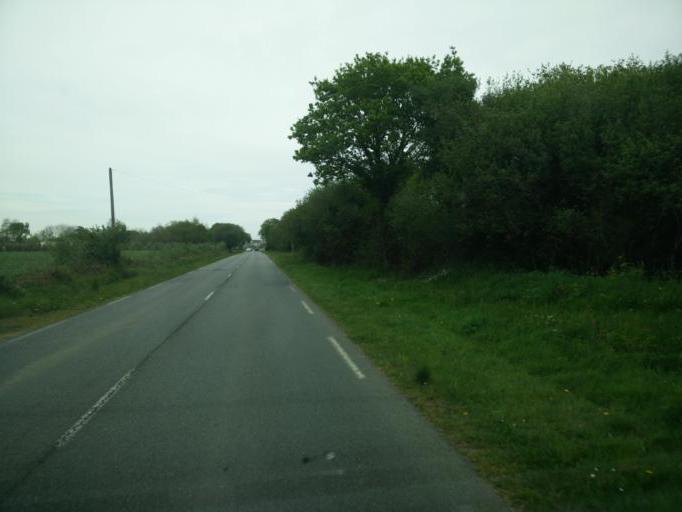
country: FR
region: Brittany
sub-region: Departement des Cotes-d'Armor
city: Pleumeur-Bodou
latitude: 48.7521
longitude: -3.5028
